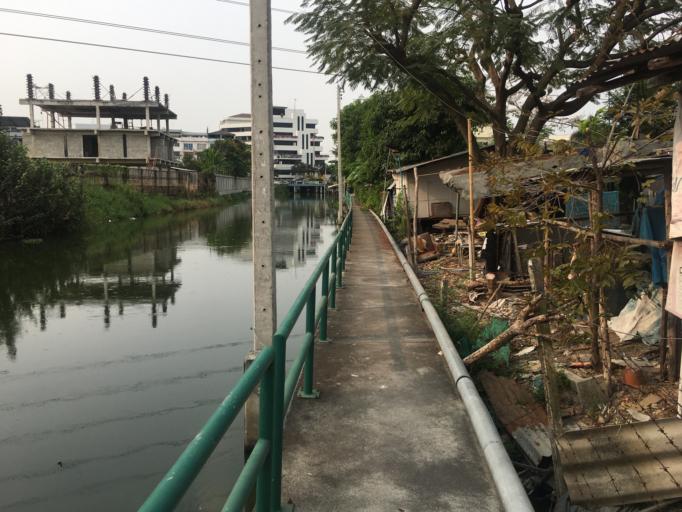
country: TH
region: Bangkok
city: Suan Luang
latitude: 13.7324
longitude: 100.6528
